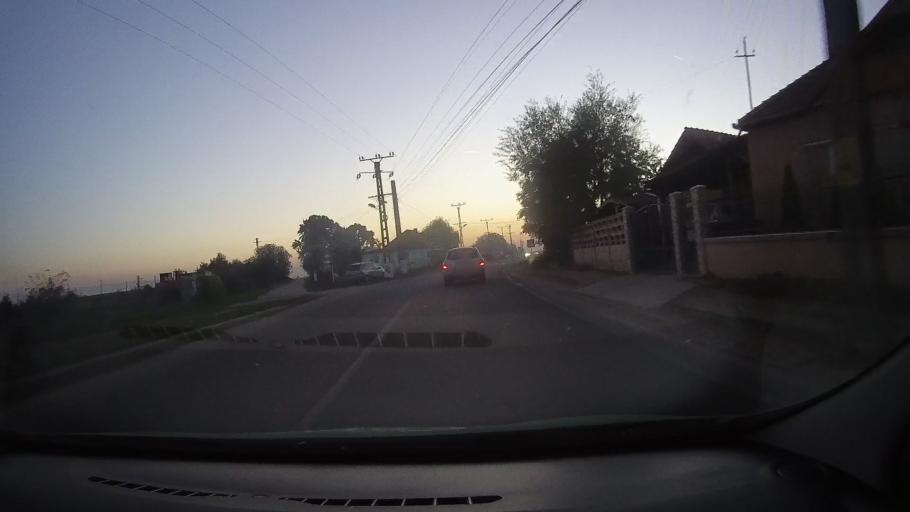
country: RO
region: Bihor
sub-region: Comuna Valea lui Mihai
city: Valea lui Mihai
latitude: 47.5119
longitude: 22.1188
